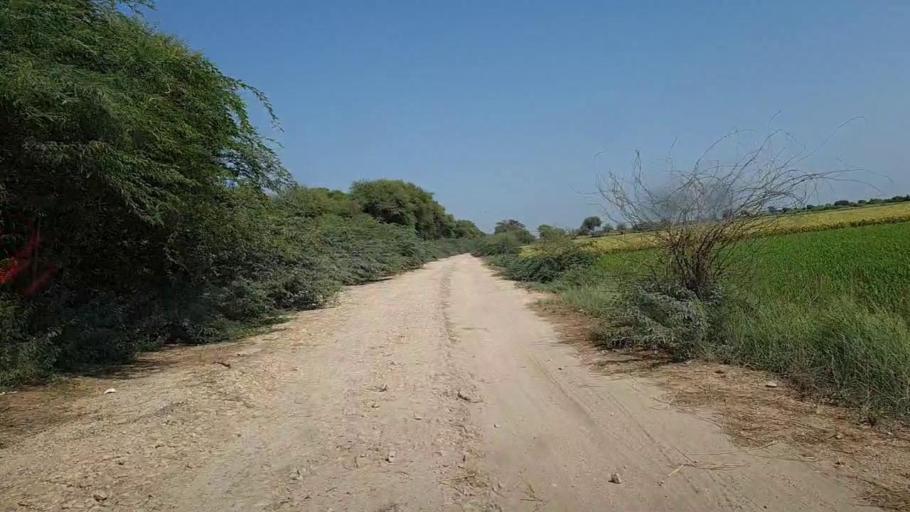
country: PK
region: Sindh
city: Mirpur Batoro
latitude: 24.7128
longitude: 68.4264
